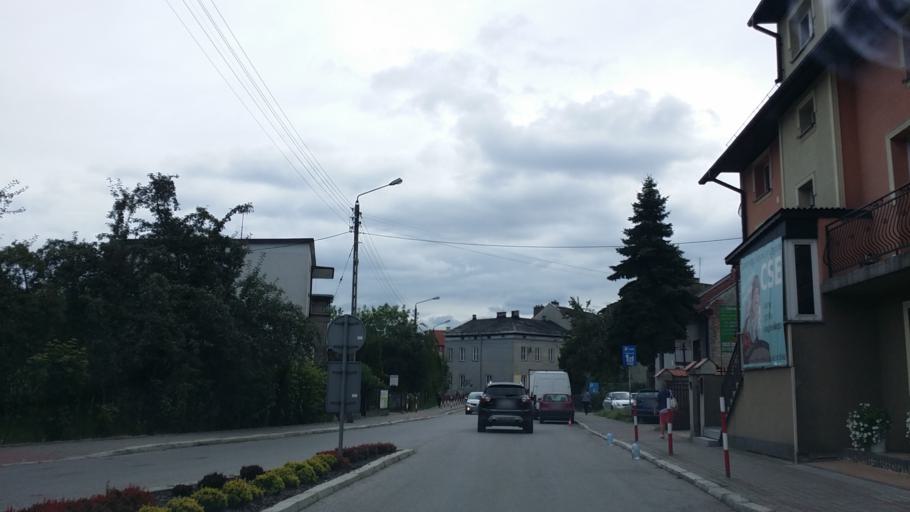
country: PL
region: Lesser Poland Voivodeship
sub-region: Powiat wadowicki
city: Wadowice
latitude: 49.8857
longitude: 19.4895
